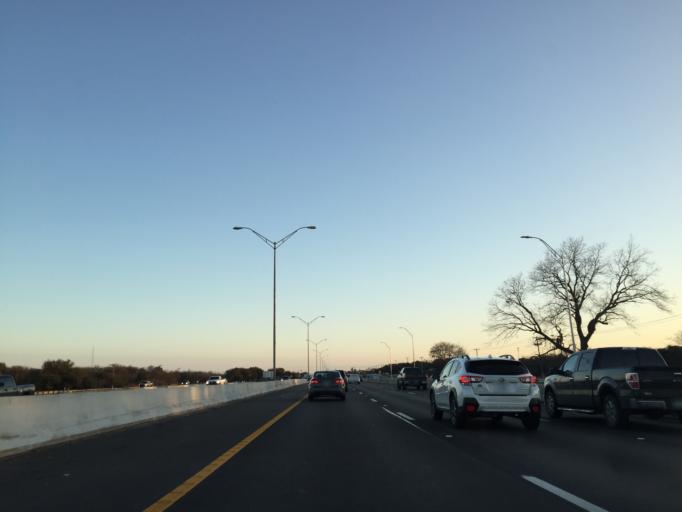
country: US
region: Texas
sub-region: Williamson County
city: Round Rock
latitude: 30.5549
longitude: -97.6925
